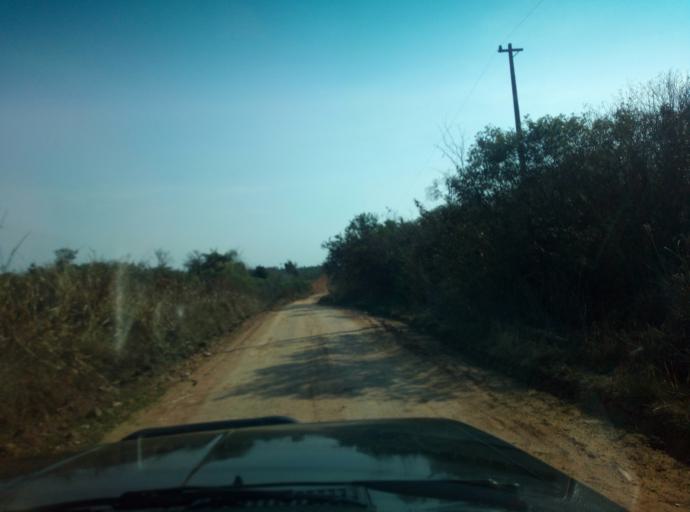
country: PY
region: Caaguazu
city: Doctor Cecilio Baez
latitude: -25.1842
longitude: -56.1919
